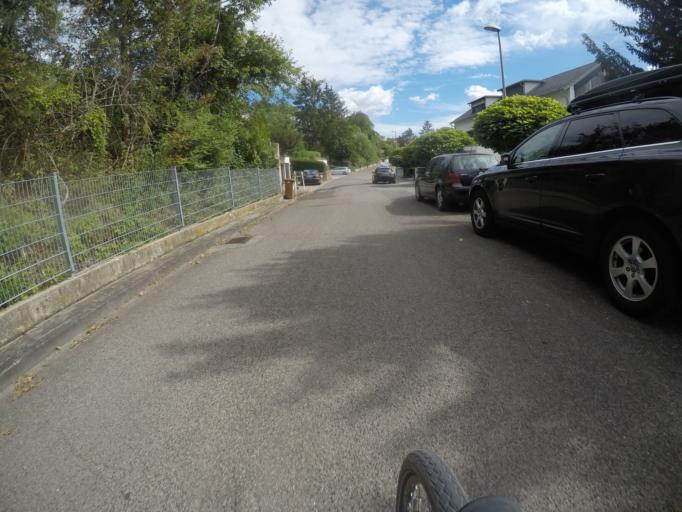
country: DE
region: Baden-Wuerttemberg
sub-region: Regierungsbezirk Stuttgart
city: Stuttgart
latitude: 48.7497
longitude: 9.1237
